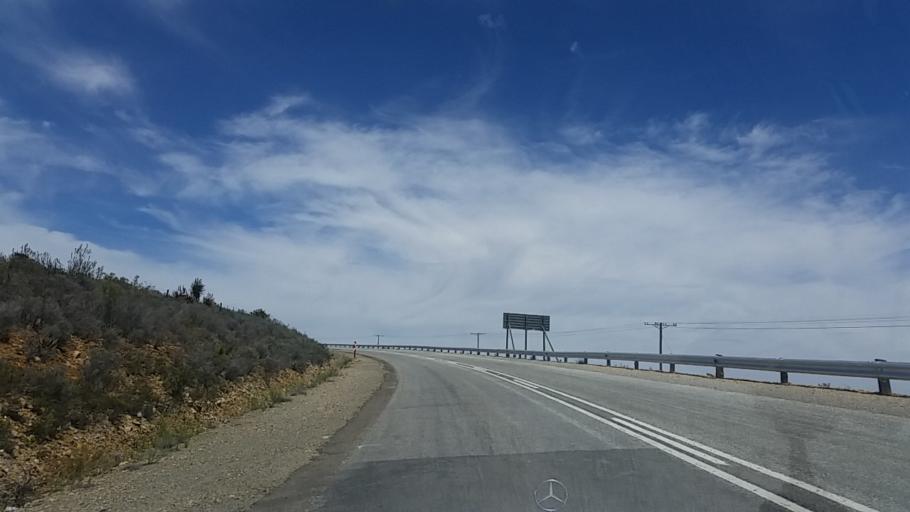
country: ZA
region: Western Cape
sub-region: Eden District Municipality
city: Knysna
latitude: -33.6292
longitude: 23.1284
